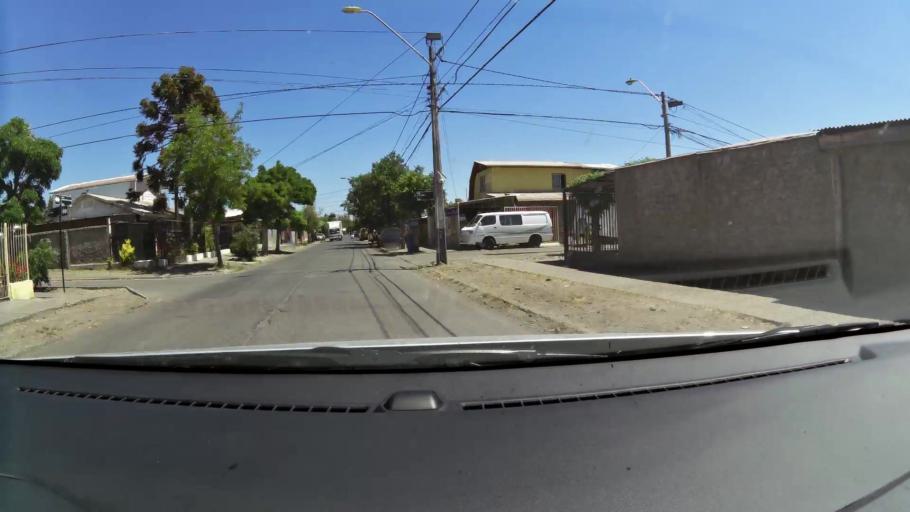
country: CL
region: Santiago Metropolitan
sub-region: Provincia de Maipo
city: San Bernardo
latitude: -33.5724
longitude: -70.6816
